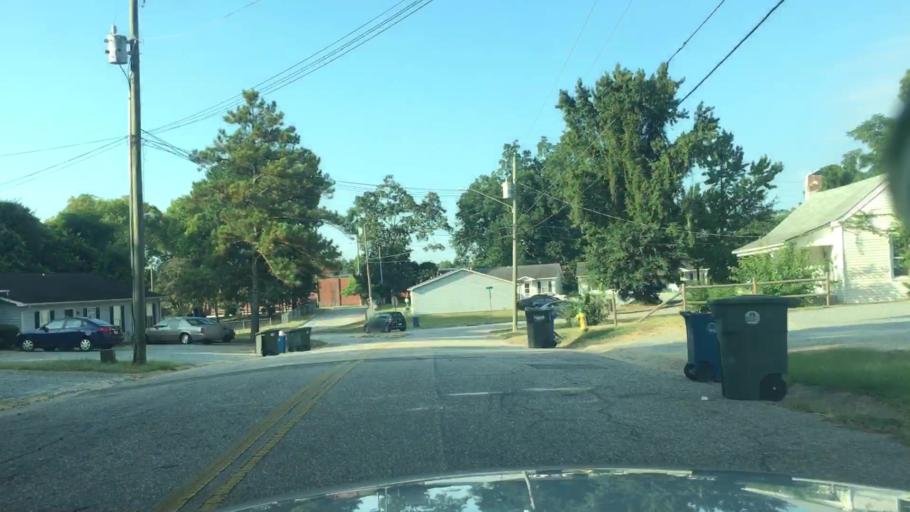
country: US
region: North Carolina
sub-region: Cumberland County
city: Fayetteville
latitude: 35.0490
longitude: -78.8912
